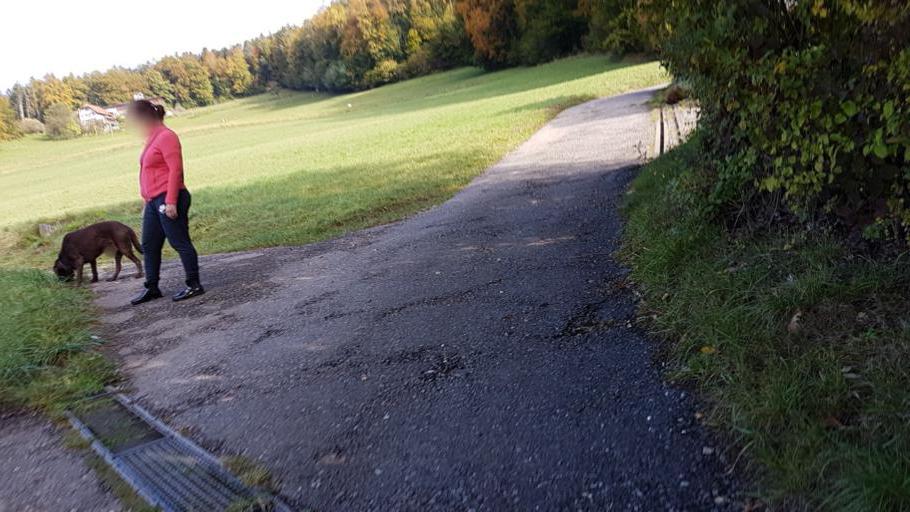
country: CH
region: Bern
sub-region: Bern-Mittelland District
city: Stettlen
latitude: 46.9334
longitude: 7.5313
